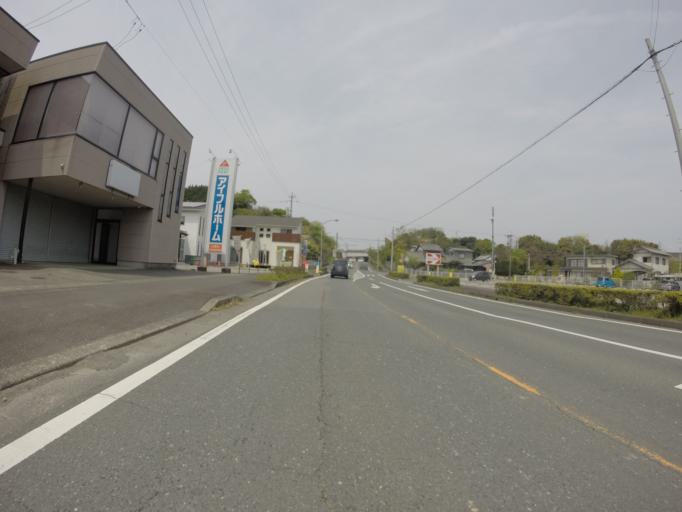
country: JP
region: Shizuoka
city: Kakegawa
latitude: 34.7625
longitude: 138.0150
